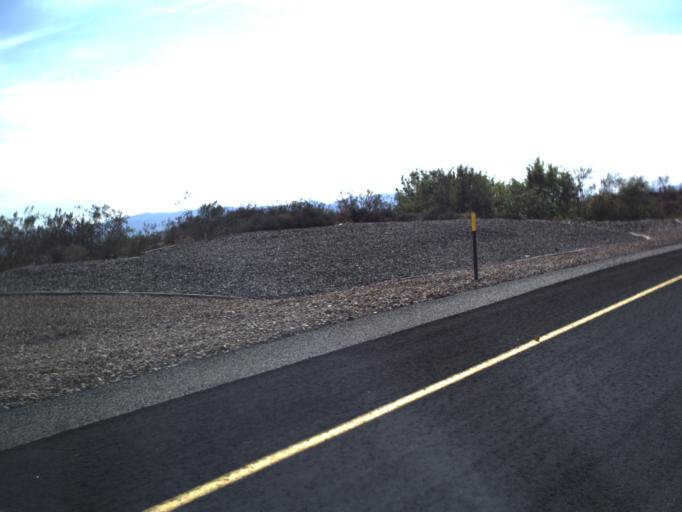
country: US
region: Utah
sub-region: Washington County
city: Washington
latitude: 37.1492
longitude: -113.4857
